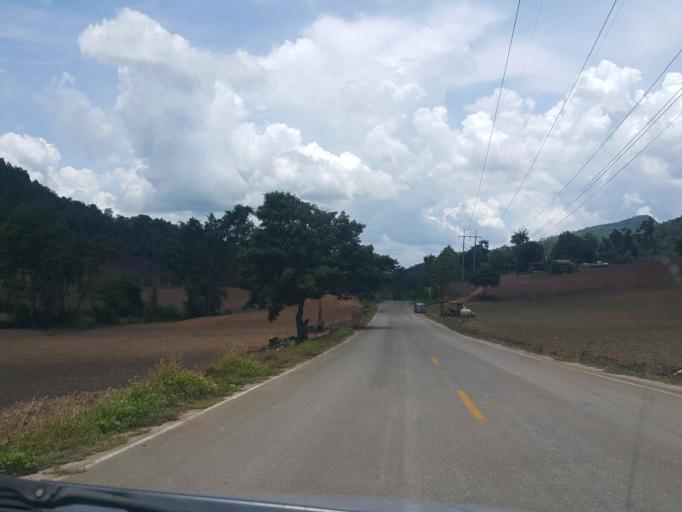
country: TH
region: Phayao
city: Chiang Muan
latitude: 18.9067
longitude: 100.1195
